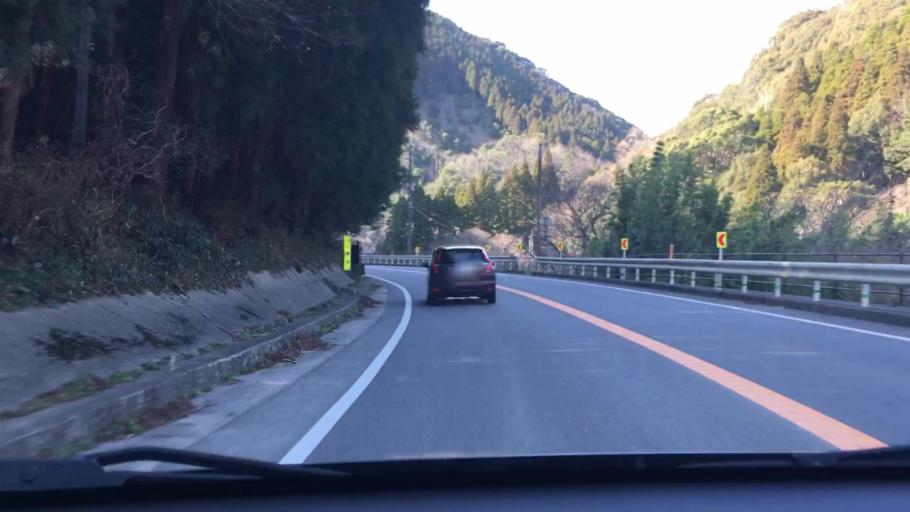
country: JP
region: Oita
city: Tsukumiura
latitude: 32.9973
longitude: 131.8192
